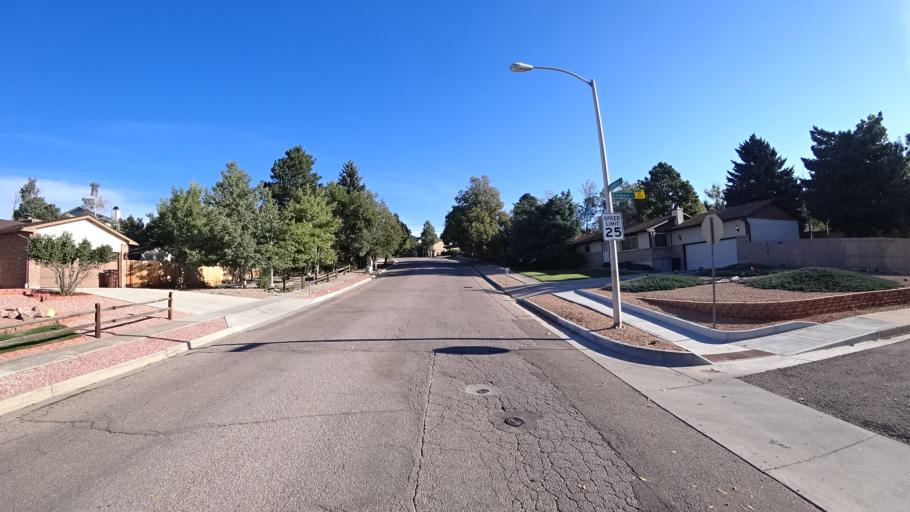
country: US
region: Colorado
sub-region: El Paso County
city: Cimarron Hills
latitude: 38.9110
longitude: -104.7552
